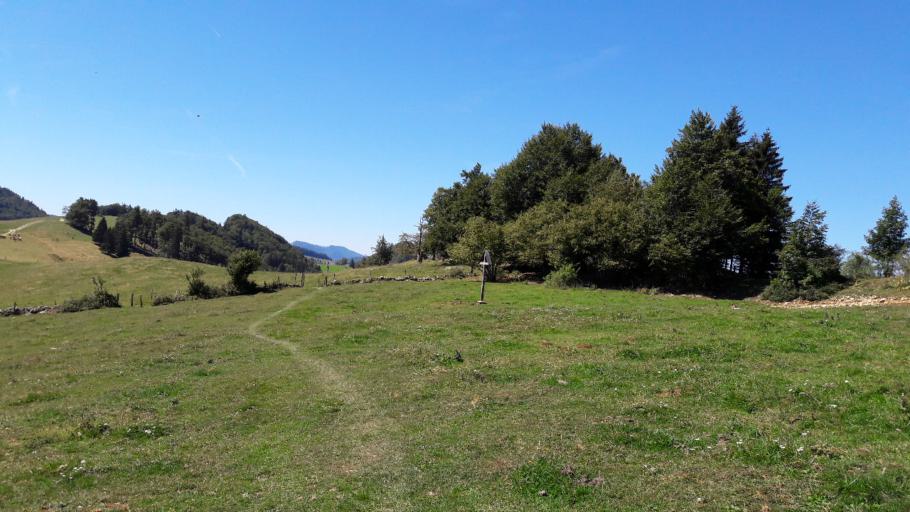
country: CH
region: Solothurn
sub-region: Bezirk Thal
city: Welschenrohr
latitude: 47.3143
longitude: 7.5686
